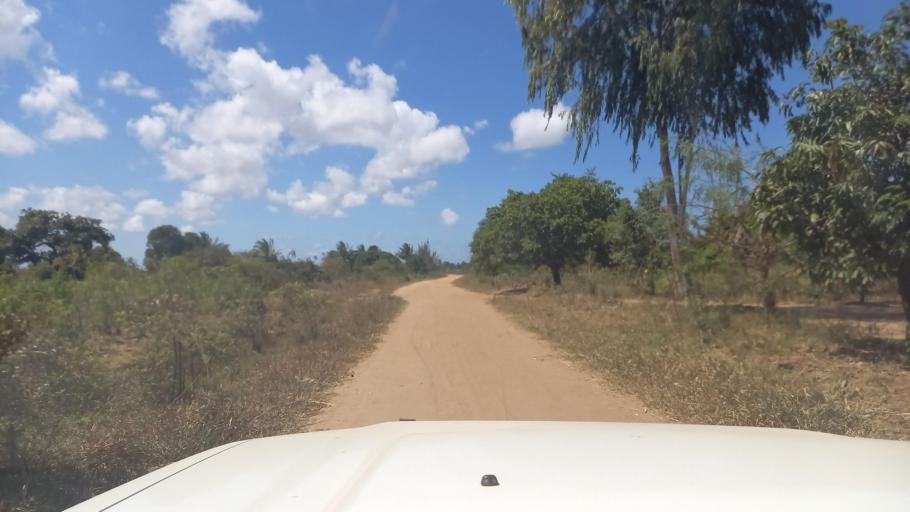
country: MZ
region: Cabo Delgado
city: Pemba
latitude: -13.4243
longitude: 40.5164
